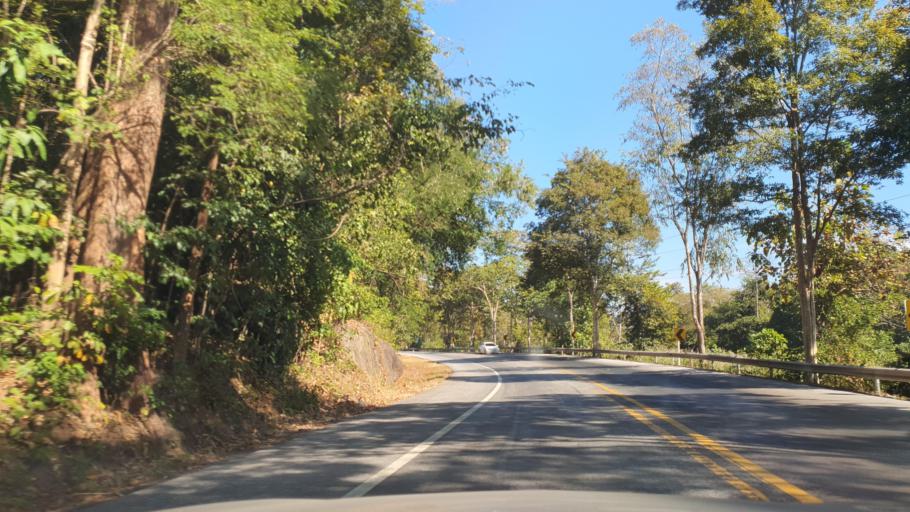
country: TH
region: Kalasin
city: Na Khu
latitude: 16.8494
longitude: 103.9261
